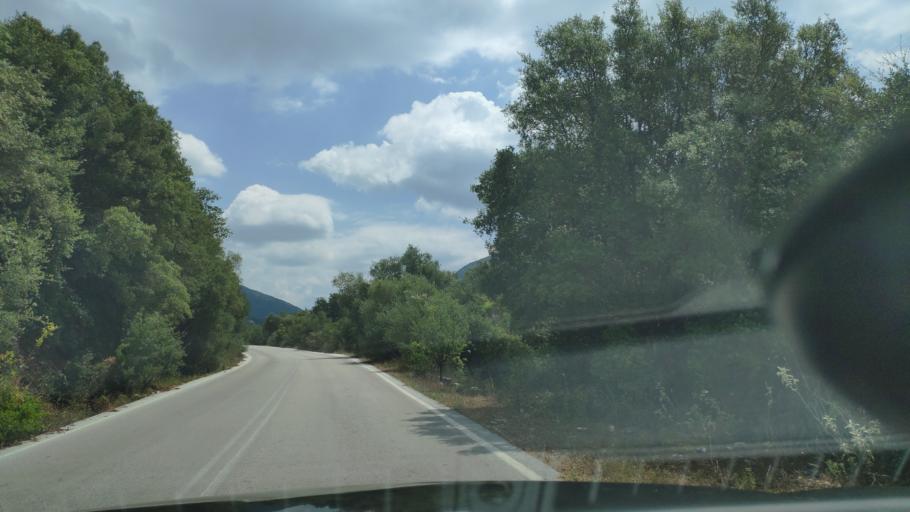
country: GR
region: Epirus
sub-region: Nomos Artas
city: Kampi
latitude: 39.2678
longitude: 20.9271
